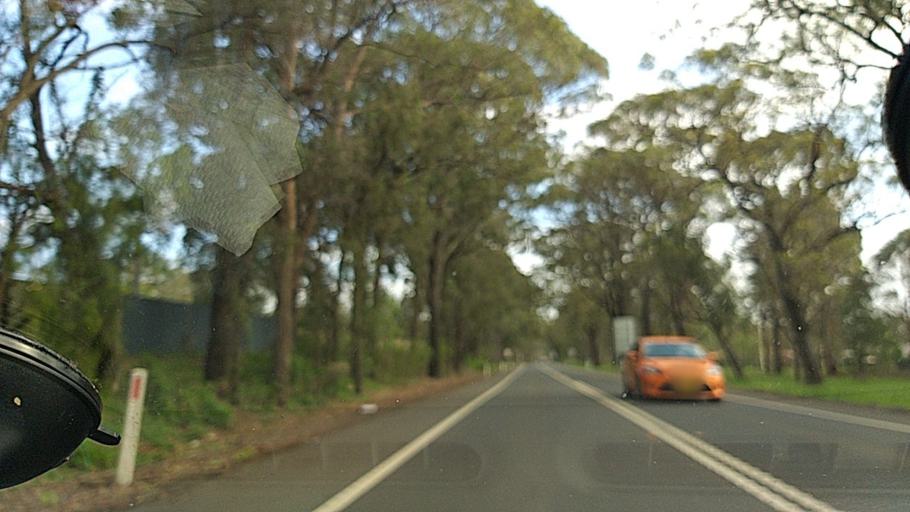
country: AU
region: New South Wales
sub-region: Campbelltown Municipality
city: Glen Alpine
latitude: -34.1154
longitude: 150.7975
